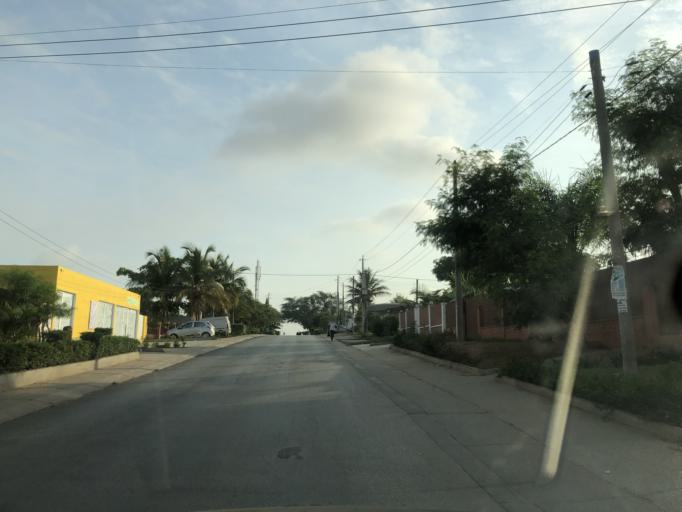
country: AO
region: Luanda
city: Luanda
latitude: -8.9006
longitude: 13.2267
